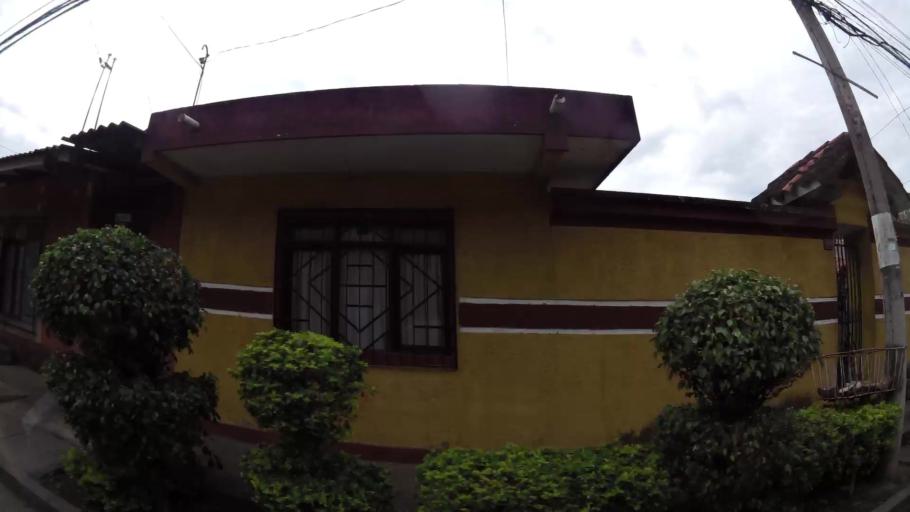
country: BO
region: Santa Cruz
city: Santa Cruz de la Sierra
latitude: -17.7554
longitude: -63.1621
